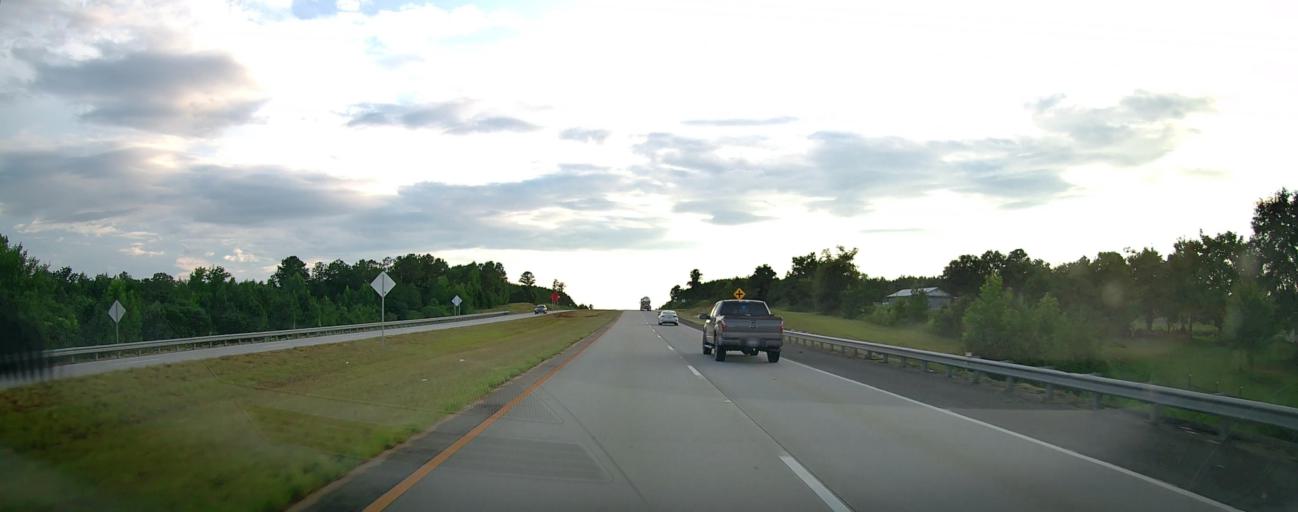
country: US
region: Georgia
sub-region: Peach County
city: Fort Valley
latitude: 32.5512
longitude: -83.9760
